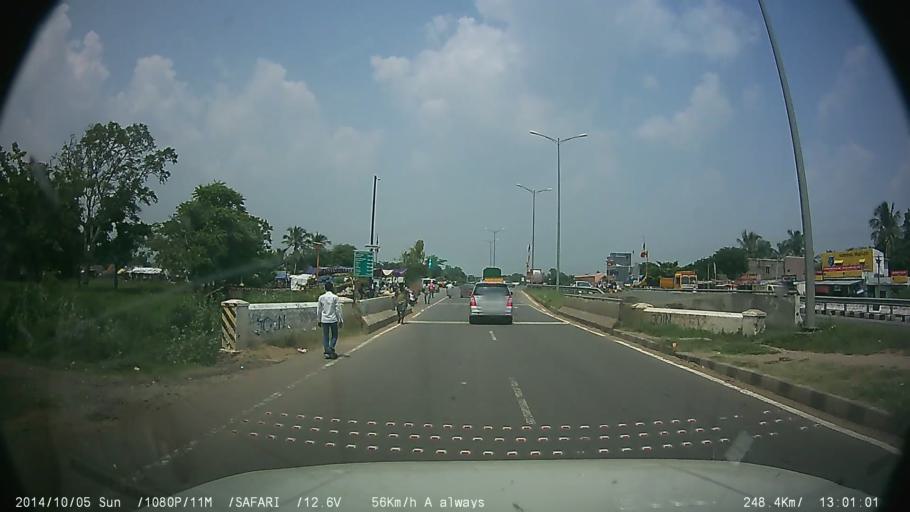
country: IN
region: Tamil Nadu
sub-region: Villupuram
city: Villupuram
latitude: 11.8338
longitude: 79.4274
